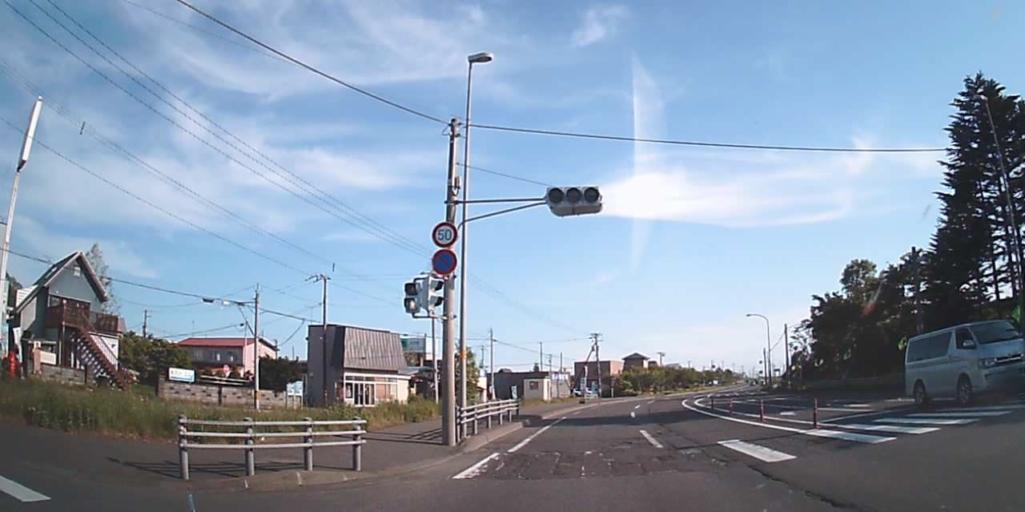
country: JP
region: Hokkaido
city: Shiraoi
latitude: 42.4514
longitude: 141.1758
